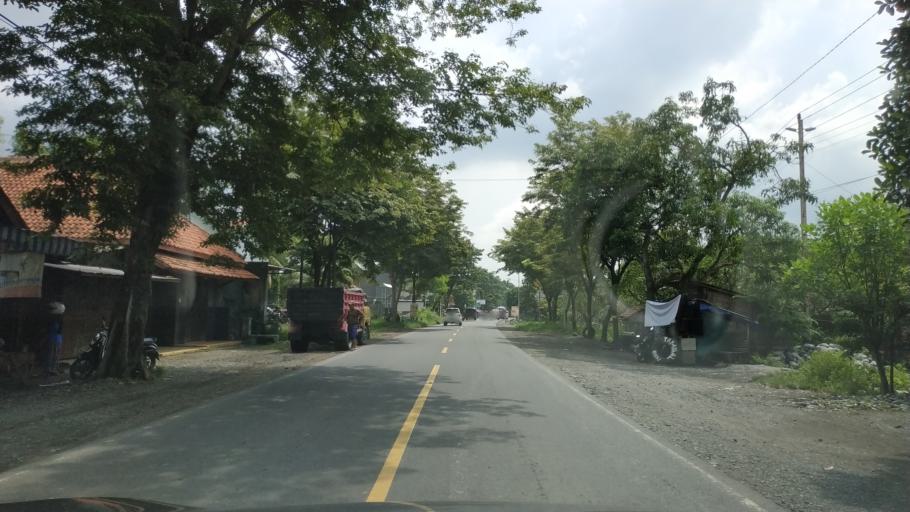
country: ID
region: Central Java
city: Lebaksiu
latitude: -7.0222
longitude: 109.1421
